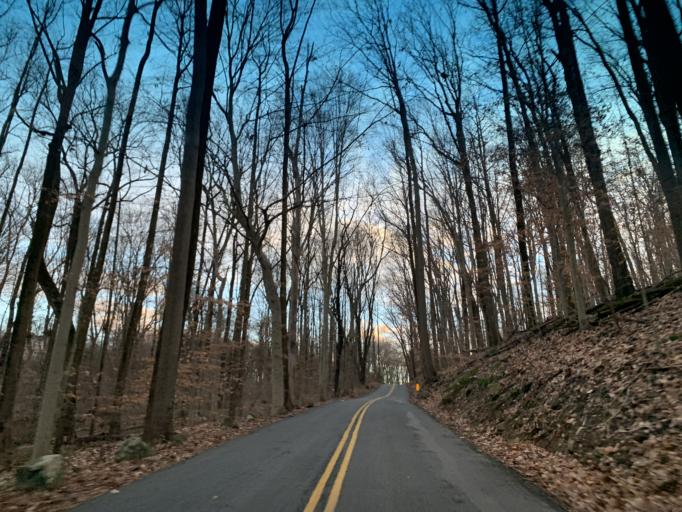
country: US
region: Maryland
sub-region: Harford County
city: Bel Air North
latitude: 39.6037
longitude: -76.3198
